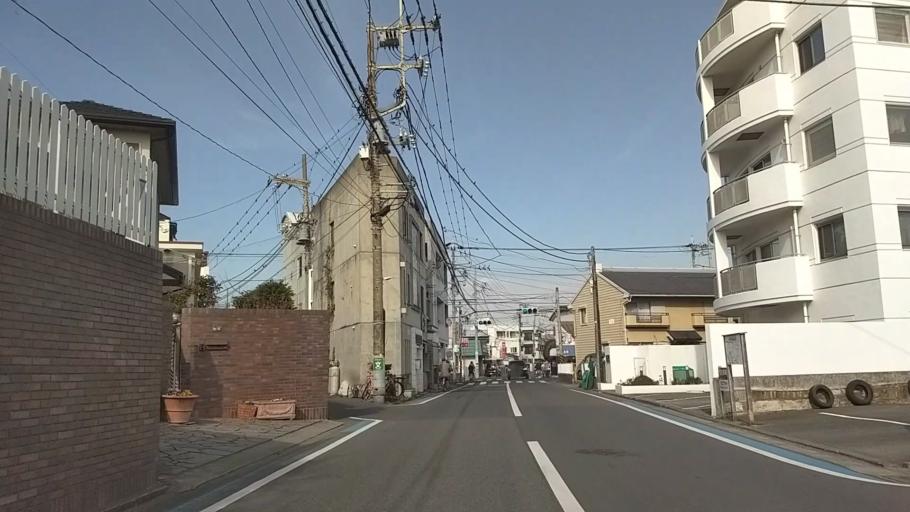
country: JP
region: Kanagawa
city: Chigasaki
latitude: 35.3238
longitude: 139.4012
